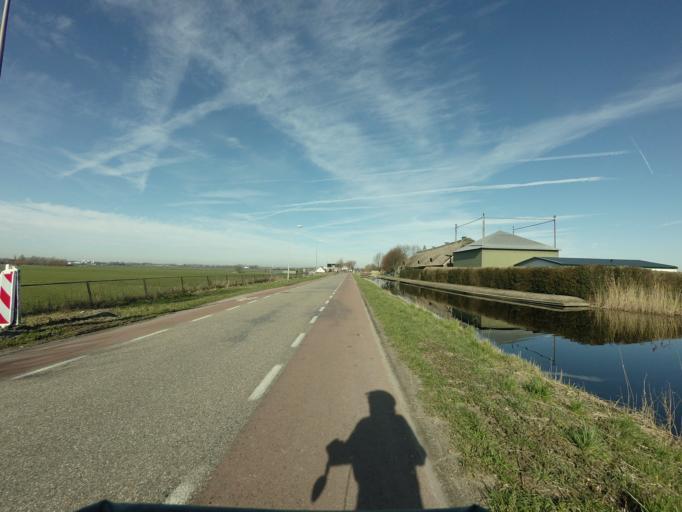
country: NL
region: South Holland
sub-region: Gemeente Kaag en Braassem
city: Leimuiden
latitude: 52.2051
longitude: 4.6691
